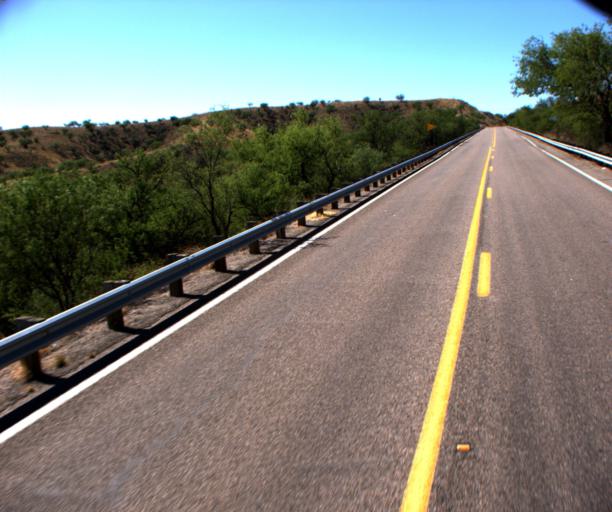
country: US
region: Arizona
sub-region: Santa Cruz County
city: Rio Rico
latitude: 31.4730
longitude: -110.8204
